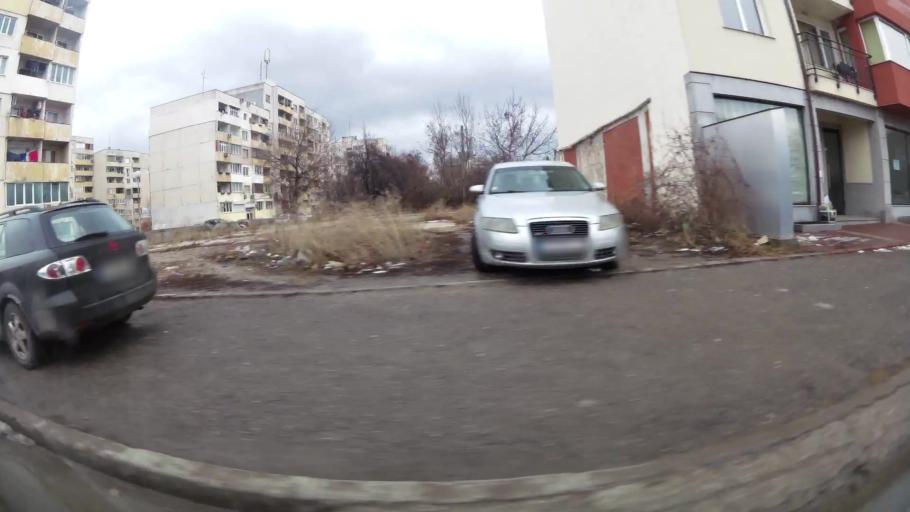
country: BG
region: Sofia-Capital
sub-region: Stolichna Obshtina
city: Sofia
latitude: 42.7250
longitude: 23.2711
